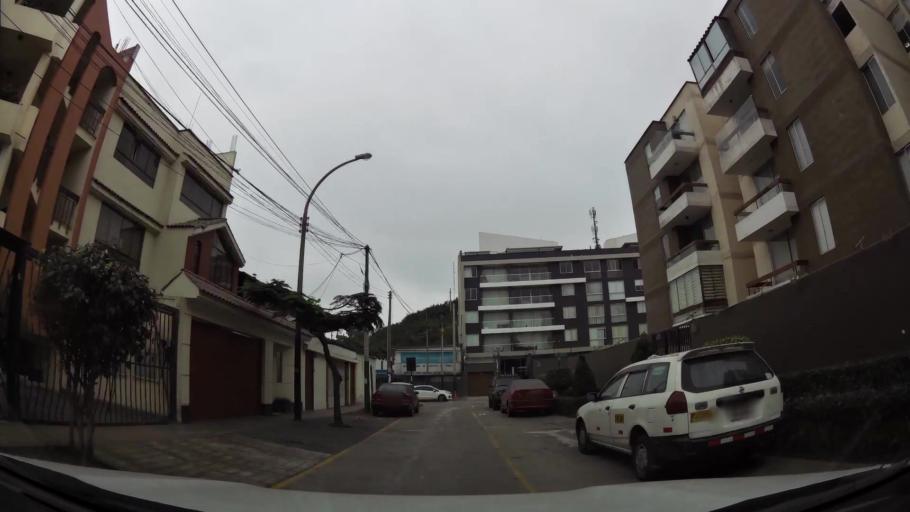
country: PE
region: Lima
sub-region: Lima
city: Surco
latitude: -12.1390
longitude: -76.9854
